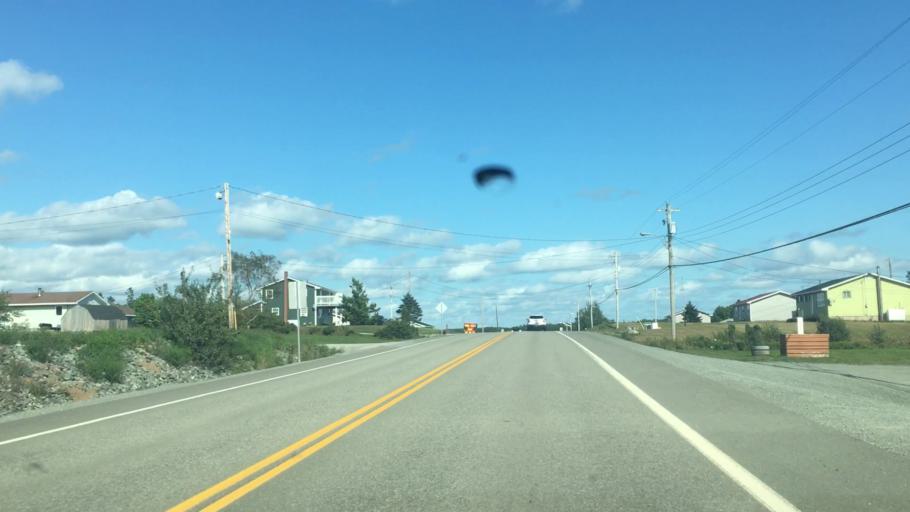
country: CA
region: Nova Scotia
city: Princeville
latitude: 45.6838
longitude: -60.7645
